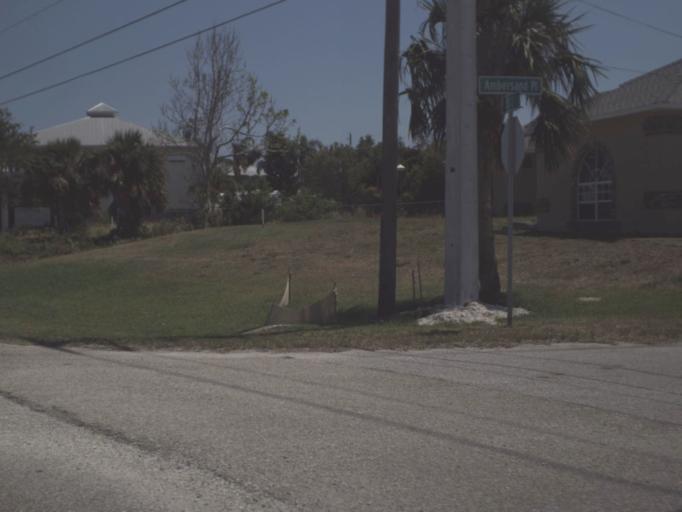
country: US
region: Florida
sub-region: Brevard County
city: Micco
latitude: 27.8988
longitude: -80.5107
